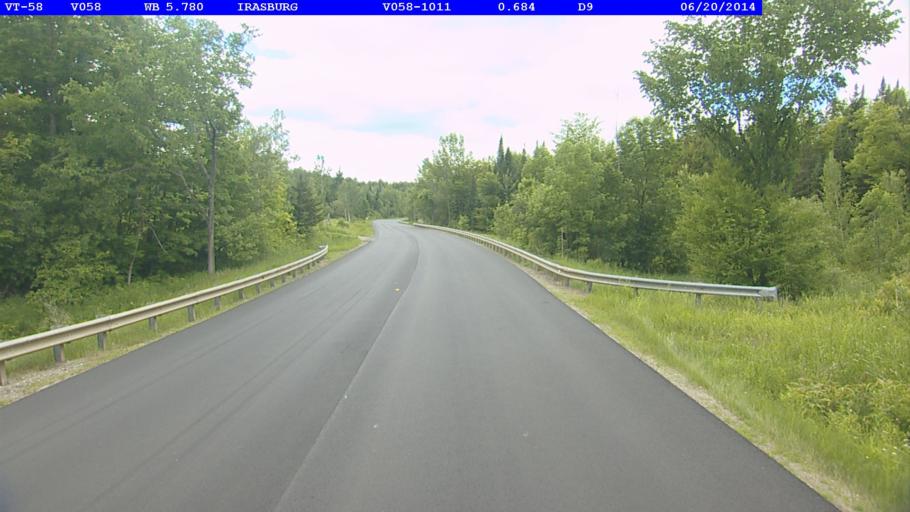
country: US
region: Vermont
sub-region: Orleans County
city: Newport
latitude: 44.8191
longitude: -72.3455
